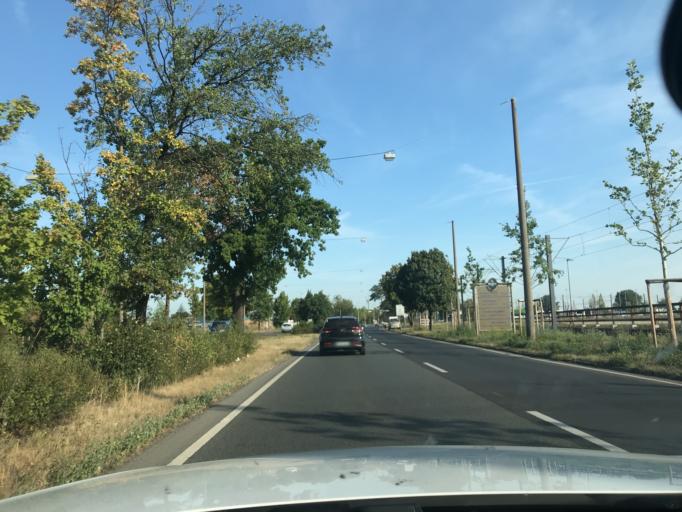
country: DE
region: Bavaria
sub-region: Regierungsbezirk Mittelfranken
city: Wetzendorf
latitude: 49.4902
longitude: 11.0544
